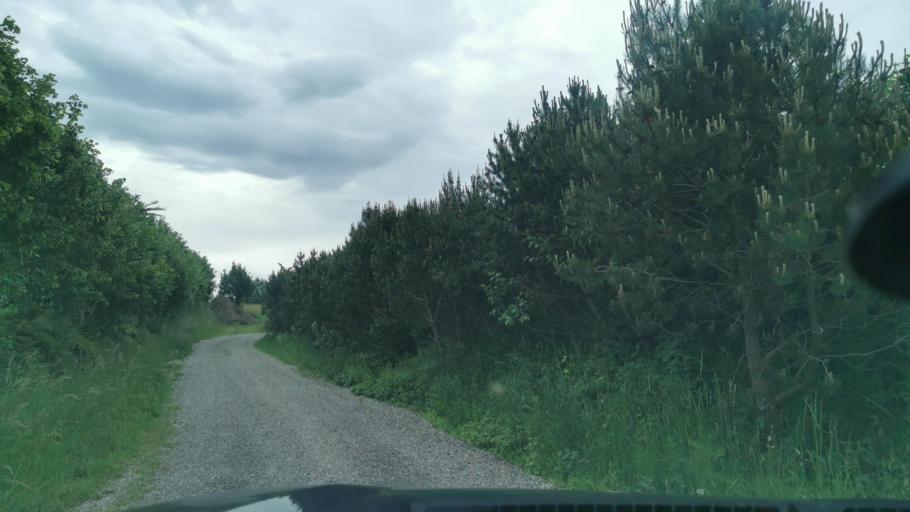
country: DK
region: Capital Region
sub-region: Hillerod Kommune
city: Hillerod
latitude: 55.9348
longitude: 12.2411
